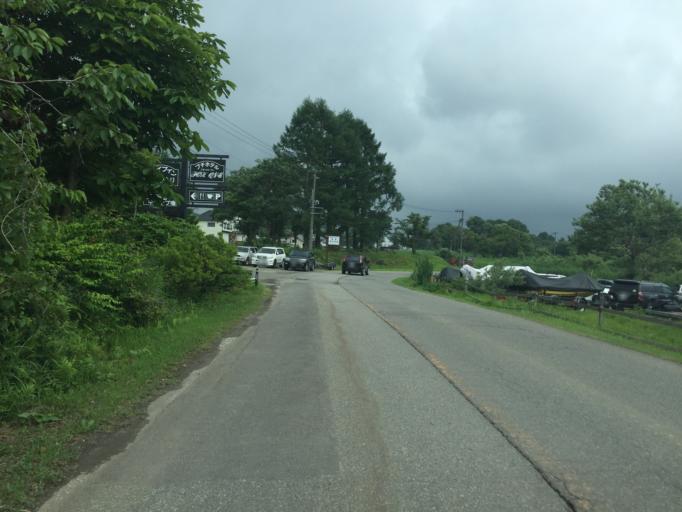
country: JP
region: Fukushima
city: Inawashiro
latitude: 37.6838
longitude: 140.0666
